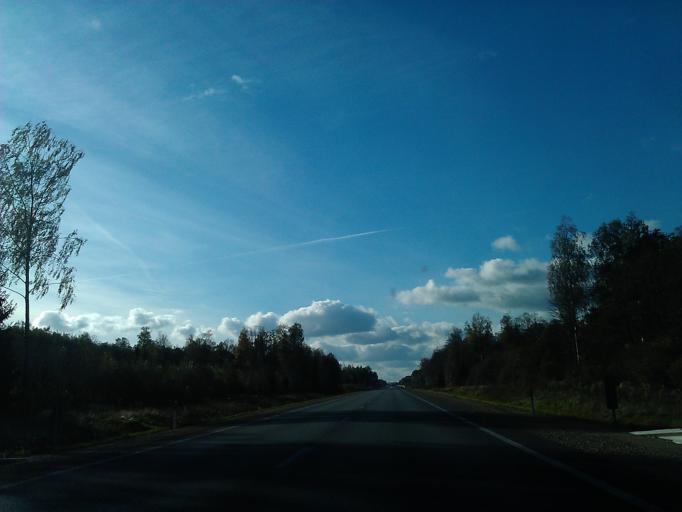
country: LV
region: Aizkraukles Rajons
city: Aizkraukle
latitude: 56.6998
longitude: 25.3092
